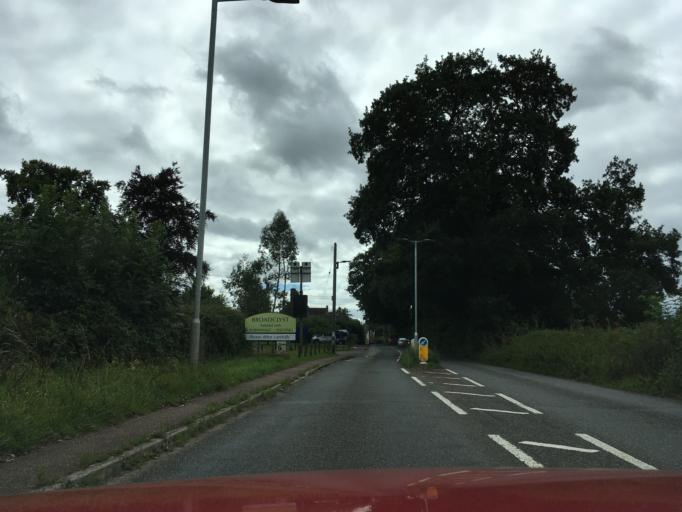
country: GB
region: England
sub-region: Devon
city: Bradninch
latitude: 50.7684
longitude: -3.4425
